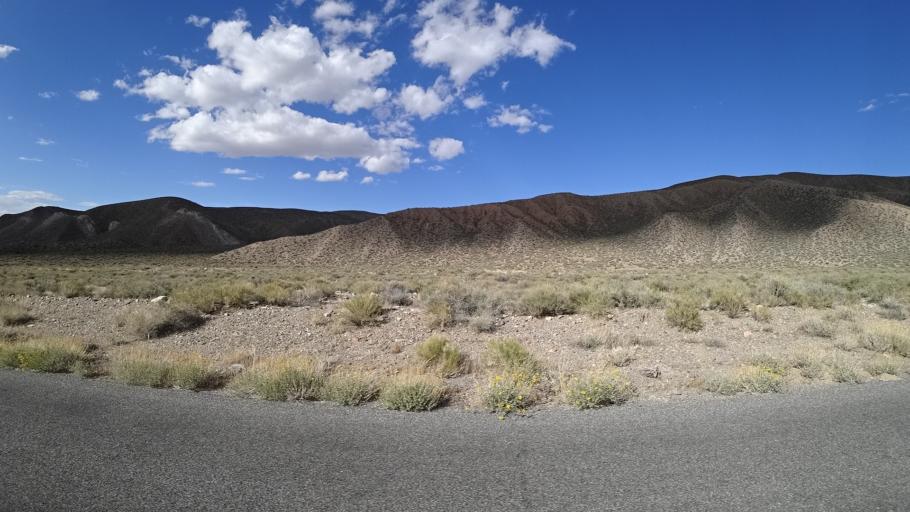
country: US
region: Nevada
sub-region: Nye County
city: Beatty
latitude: 36.4024
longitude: -117.1675
